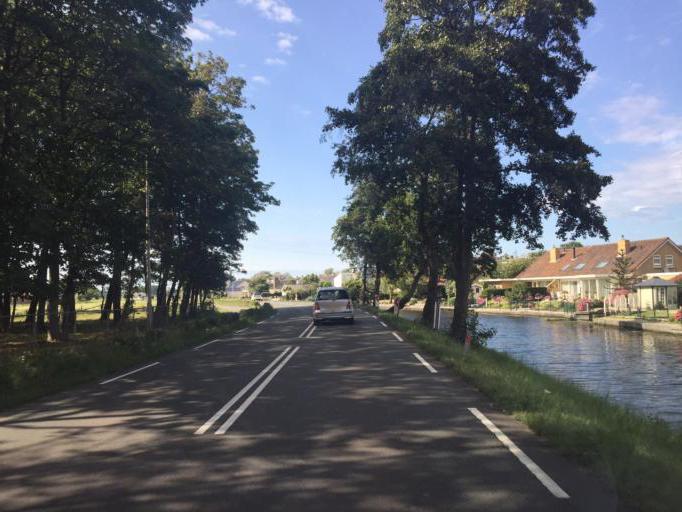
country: NL
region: South Holland
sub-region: Gemeente Teylingen
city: Voorhout
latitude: 52.2210
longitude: 4.4765
